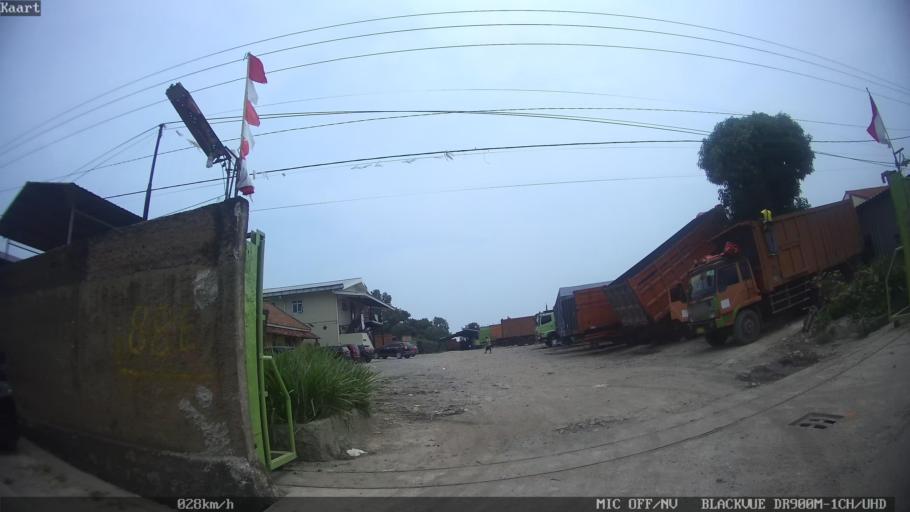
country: ID
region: Lampung
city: Bandarlampung
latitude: -5.4066
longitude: 105.3079
